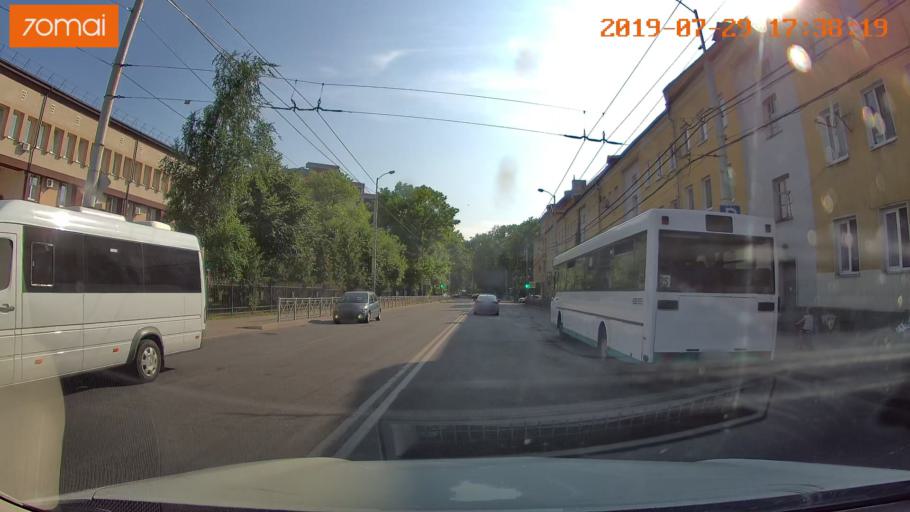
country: RU
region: Kaliningrad
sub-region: Gorod Kaliningrad
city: Kaliningrad
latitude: 54.7239
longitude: 20.5089
